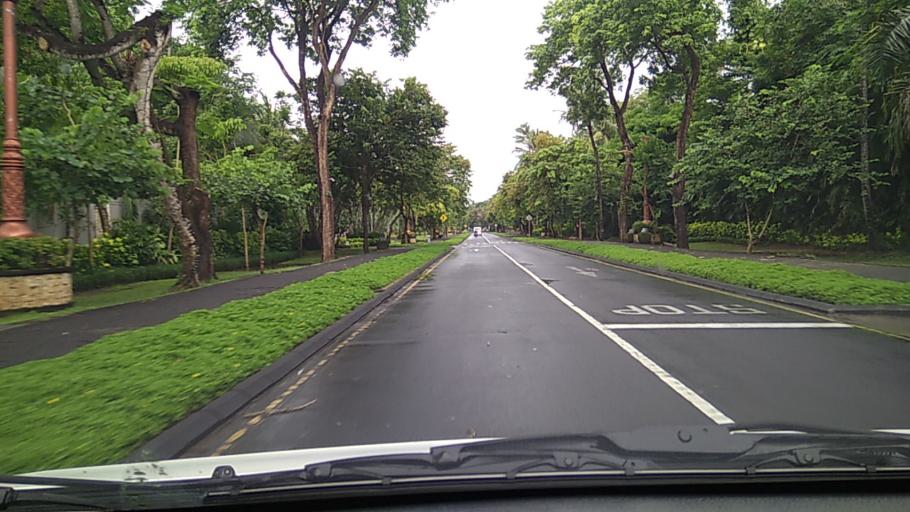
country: ID
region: Bali
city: Bualu
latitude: -8.7922
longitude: 115.2273
